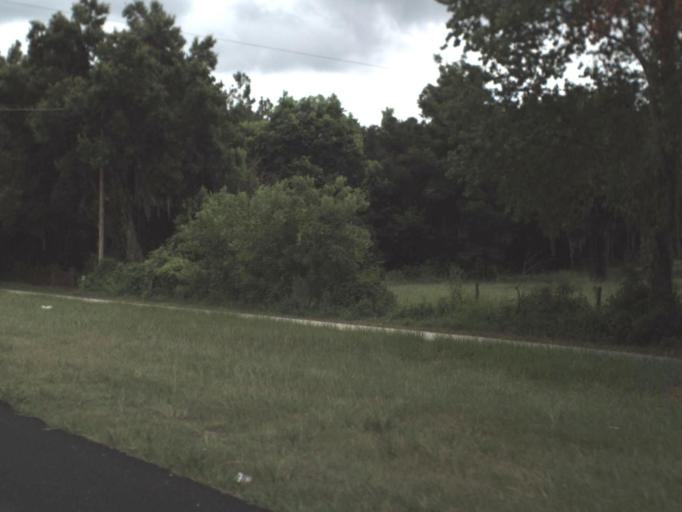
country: US
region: Florida
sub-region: Pasco County
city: Dade City North
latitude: 28.4050
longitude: -82.1945
